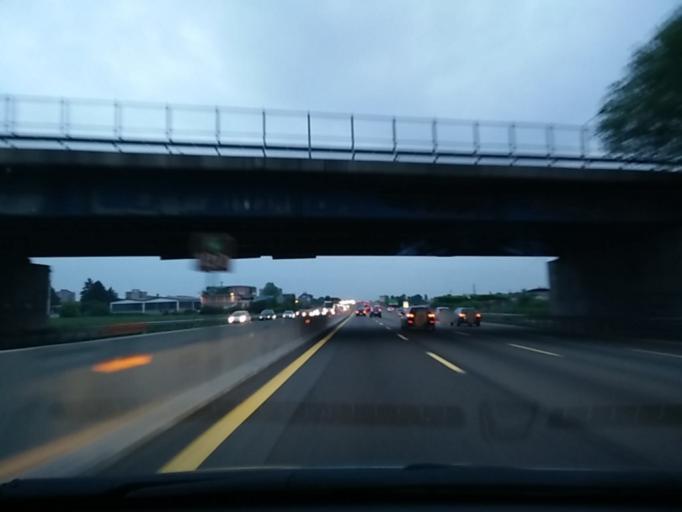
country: IT
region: Lombardy
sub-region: Citta metropolitana di Milano
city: Novate Milanese
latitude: 45.5222
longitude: 9.1339
